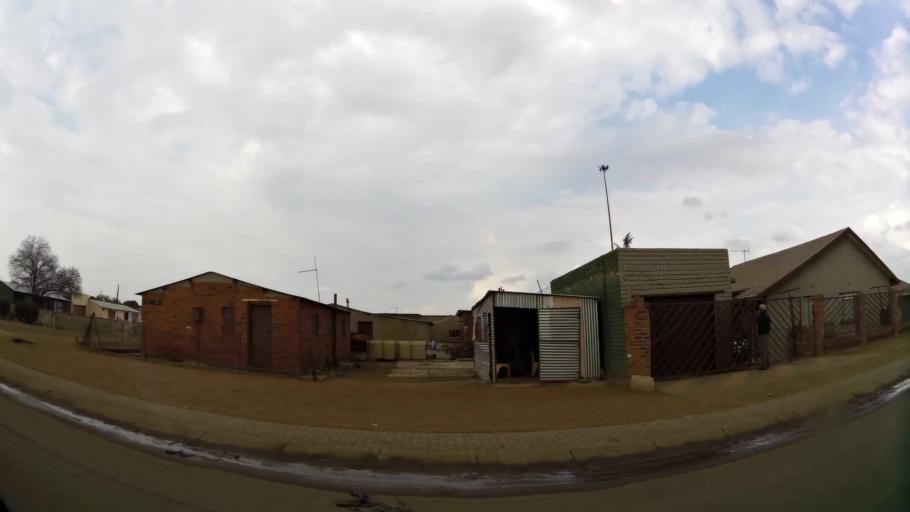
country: ZA
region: Gauteng
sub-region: Sedibeng District Municipality
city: Vanderbijlpark
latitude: -26.6635
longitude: 27.8513
